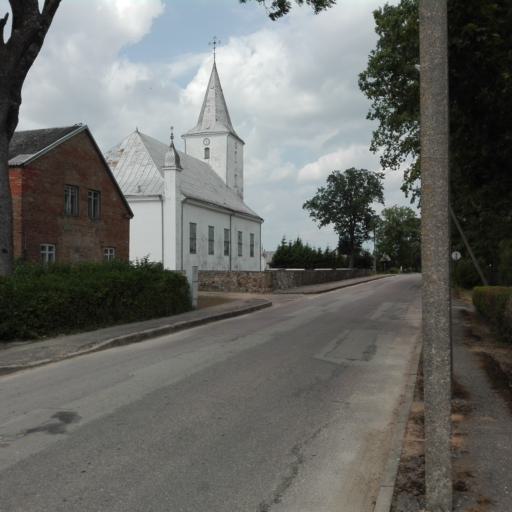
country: LT
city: Obeliai
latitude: 56.1185
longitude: 25.0045
